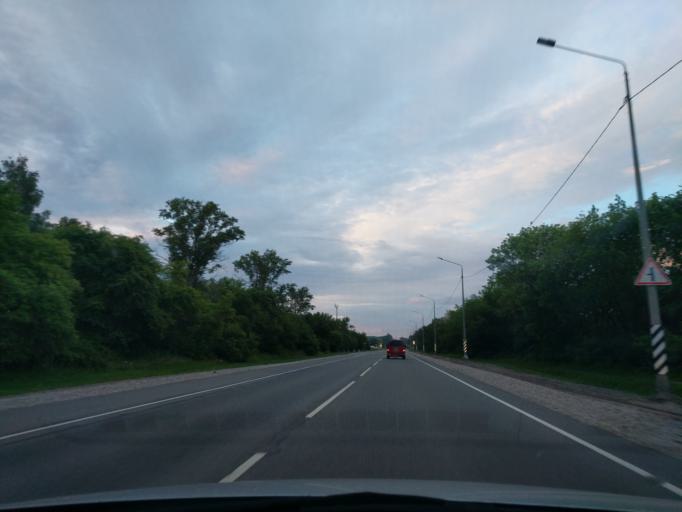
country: RU
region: Kaluga
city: Obninsk
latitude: 55.0668
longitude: 36.6016
